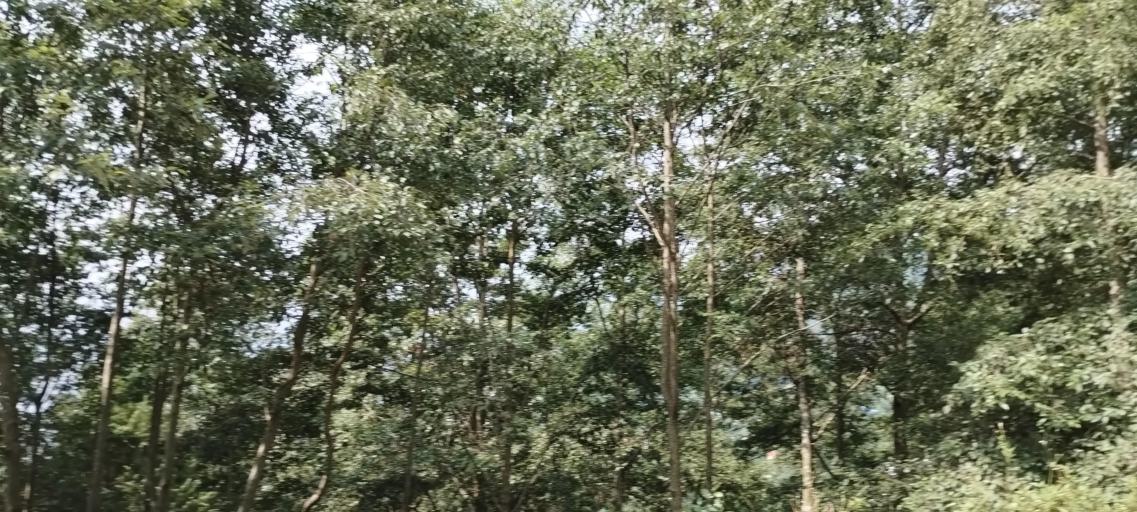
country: NP
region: Central Region
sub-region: Bagmati Zone
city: Kathmandu
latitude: 27.7907
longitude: 85.3599
